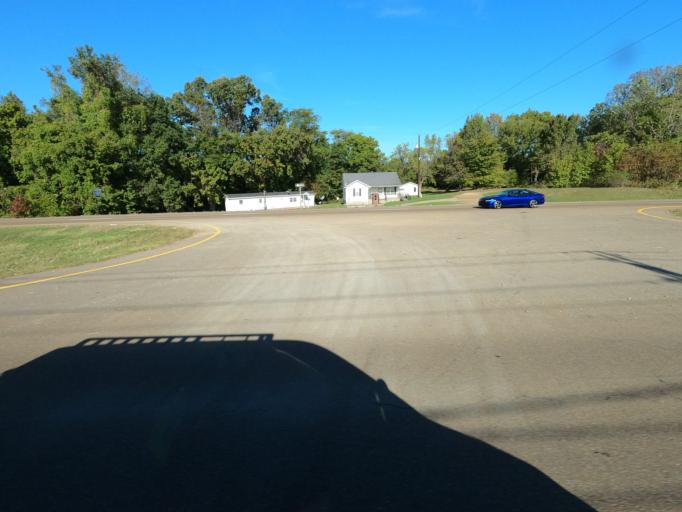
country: US
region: Tennessee
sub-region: Tipton County
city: Brighton
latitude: 35.4721
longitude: -89.7501
